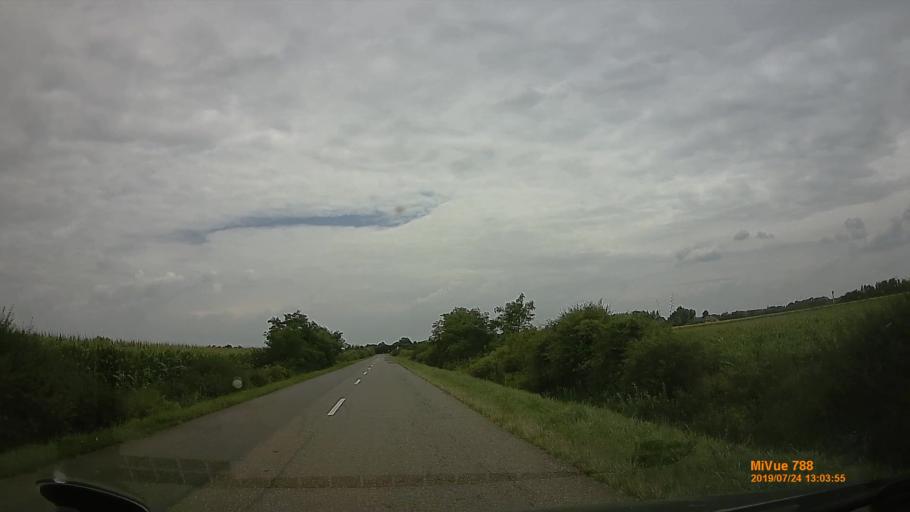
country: HU
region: Szabolcs-Szatmar-Bereg
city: Aranyosapati
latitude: 48.2066
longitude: 22.3038
